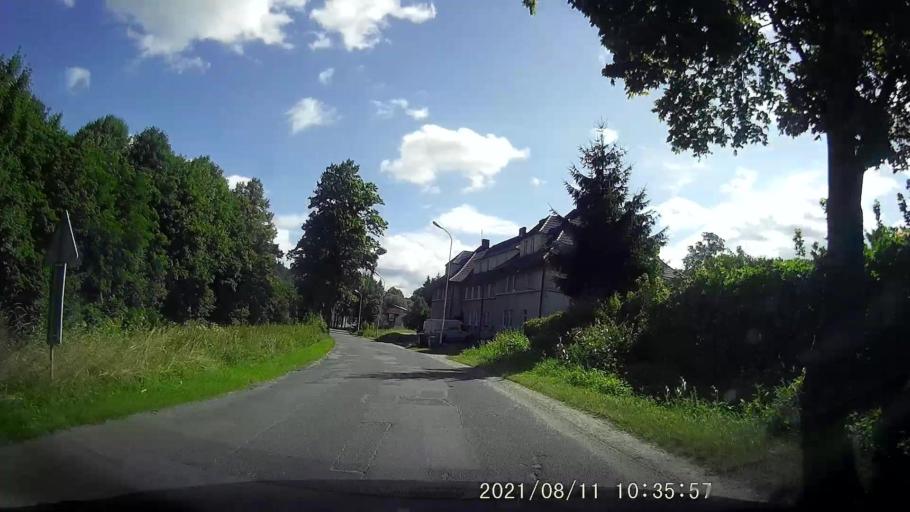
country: PL
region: Lower Silesian Voivodeship
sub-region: Powiat klodzki
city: Szczytna
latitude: 50.4018
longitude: 16.4595
